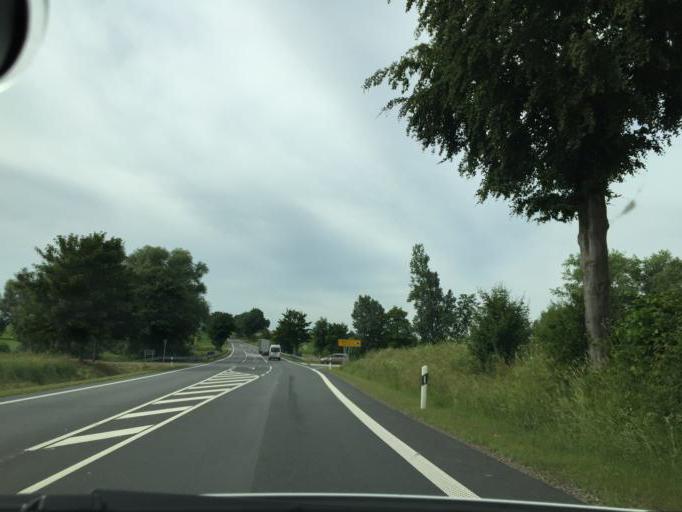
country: DE
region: North Rhine-Westphalia
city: Warburg
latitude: 51.5535
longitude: 9.1324
